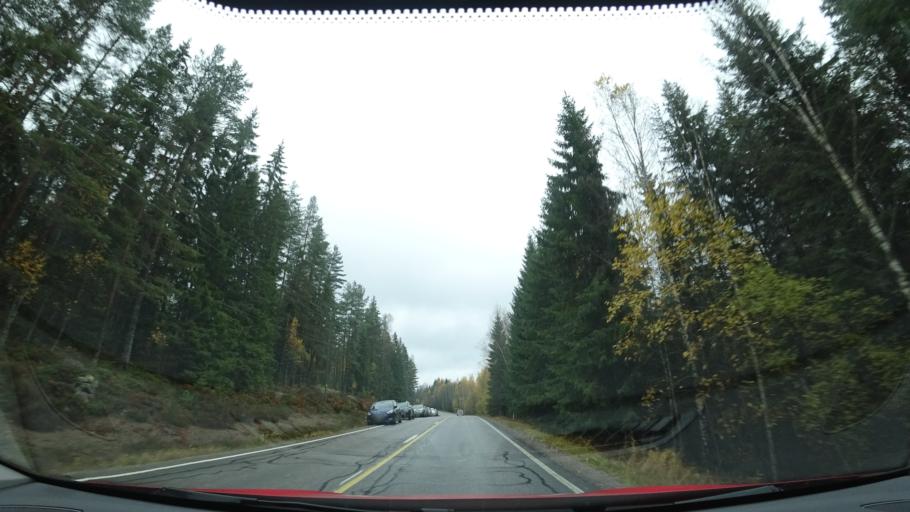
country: FI
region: Uusimaa
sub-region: Helsinki
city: Sibbo
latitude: 60.2853
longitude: 25.1968
